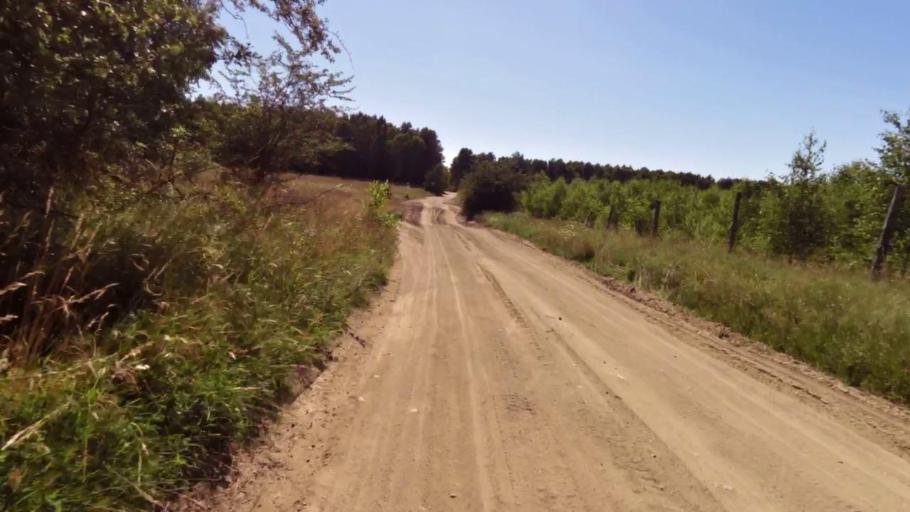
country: PL
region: West Pomeranian Voivodeship
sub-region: Powiat szczecinecki
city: Bialy Bor
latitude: 53.8684
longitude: 16.7876
